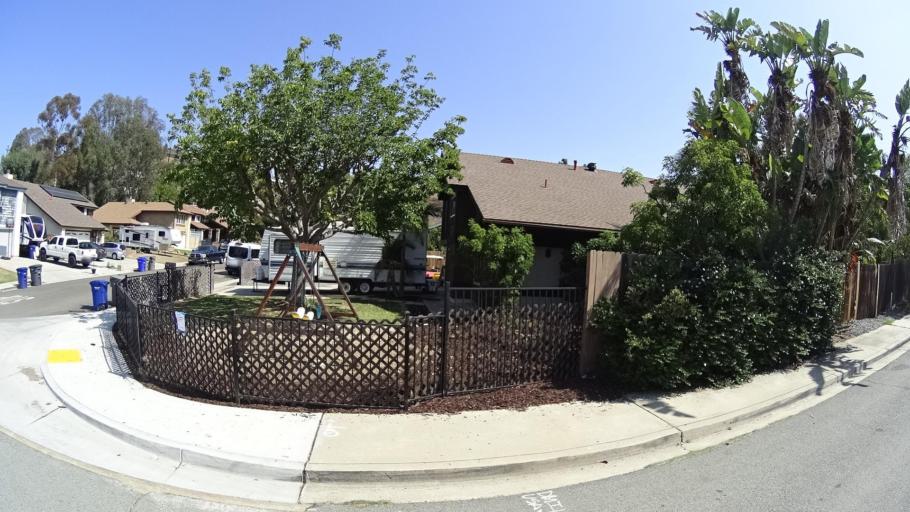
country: US
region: California
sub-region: San Diego County
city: Spring Valley
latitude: 32.7418
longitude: -116.9884
